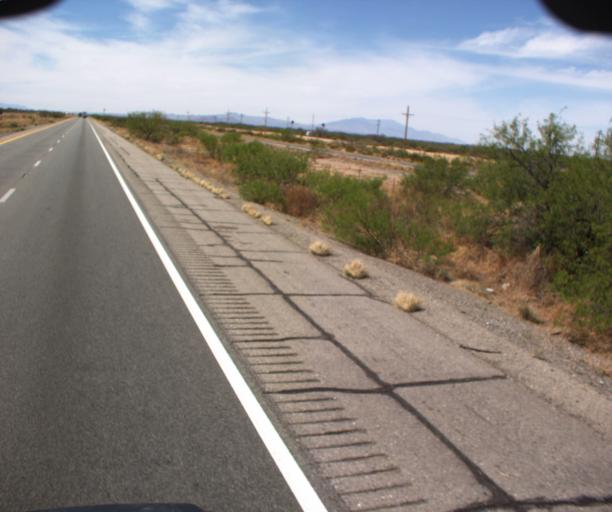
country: US
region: Arizona
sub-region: Cochise County
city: Willcox
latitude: 32.3004
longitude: -109.3665
